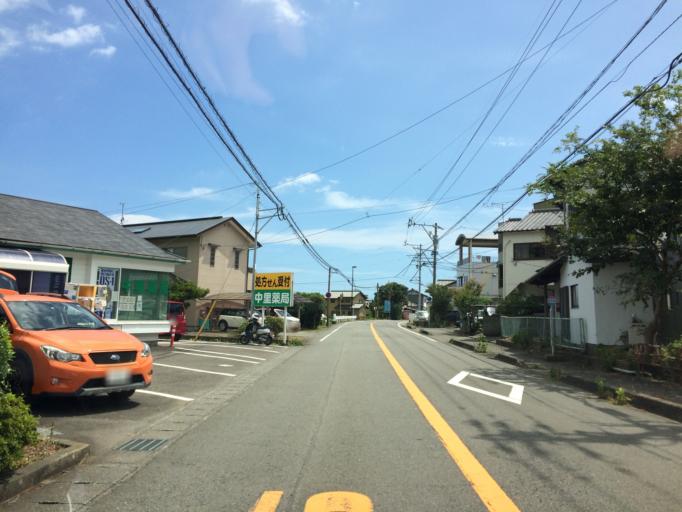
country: JP
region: Shizuoka
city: Yaizu
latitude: 34.8861
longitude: 138.3128
